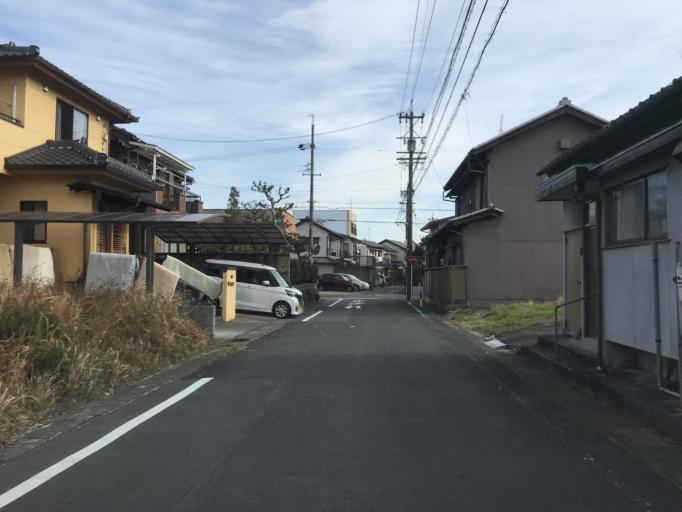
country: JP
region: Aichi
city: Inazawa
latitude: 35.2202
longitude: 136.8353
